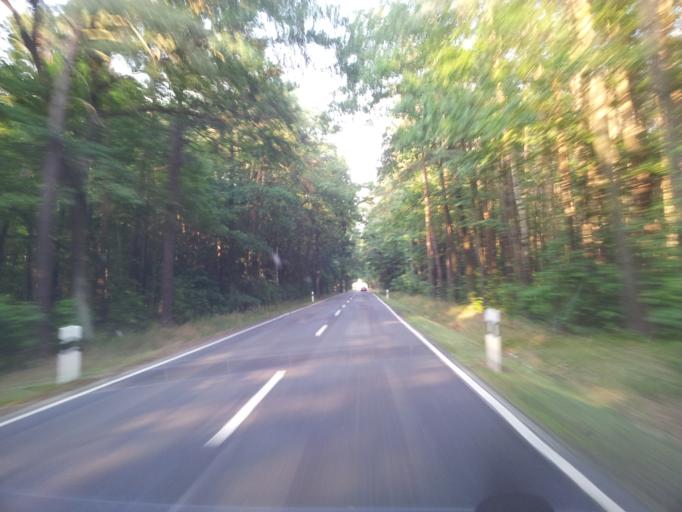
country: DE
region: Saxony
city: Schwepnitz
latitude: 51.3450
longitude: 14.0048
